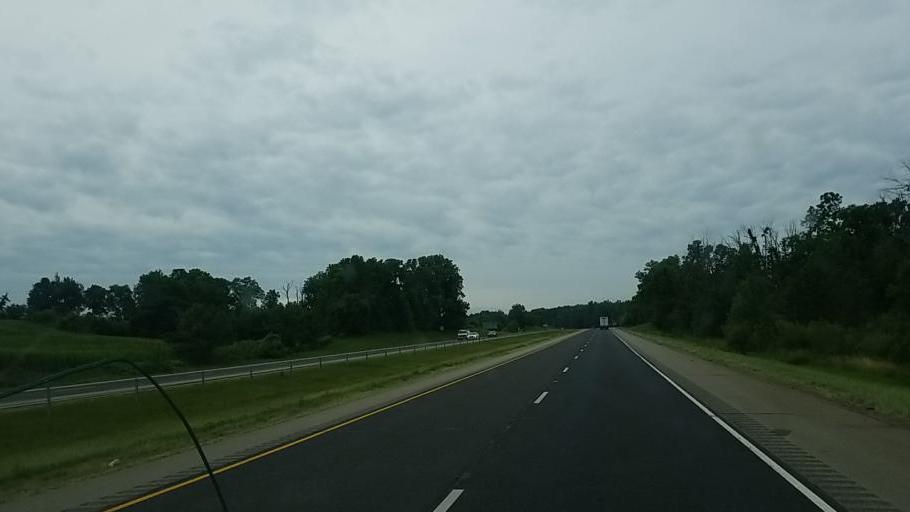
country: US
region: Indiana
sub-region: Steuben County
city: Angola
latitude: 41.6517
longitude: -85.0437
